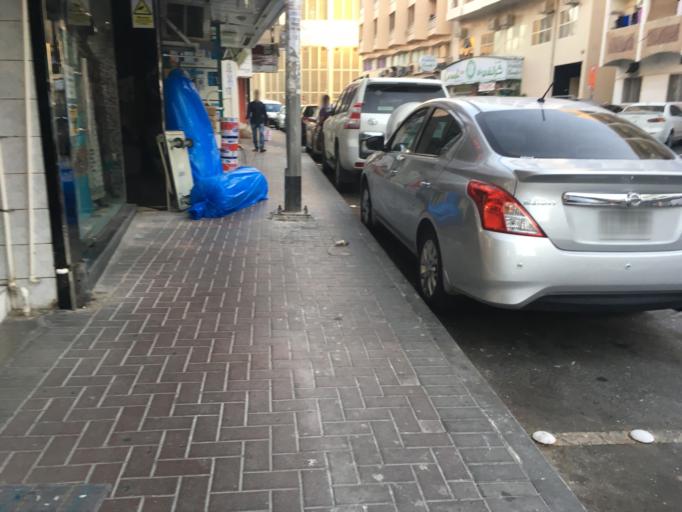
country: AE
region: Ash Shariqah
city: Sharjah
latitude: 25.2623
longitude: 55.2986
